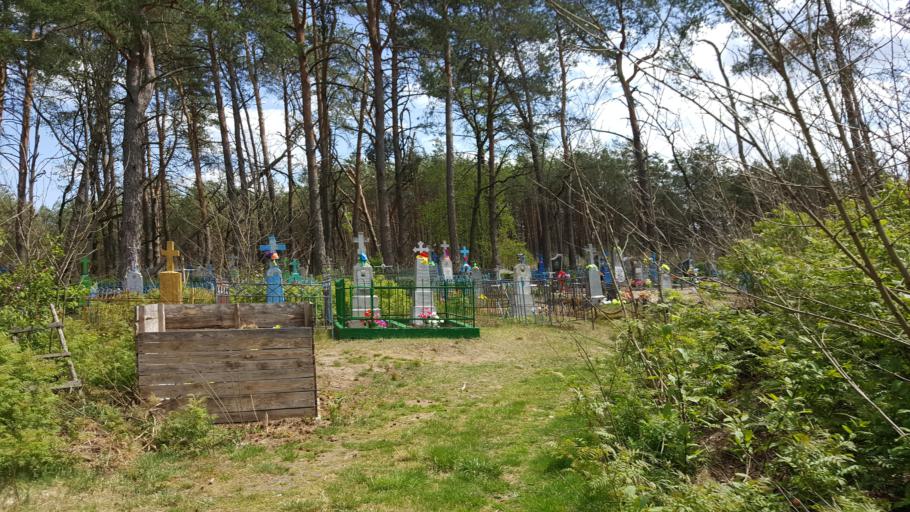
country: BY
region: Brest
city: Zhabinka
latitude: 52.4090
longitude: 24.0916
